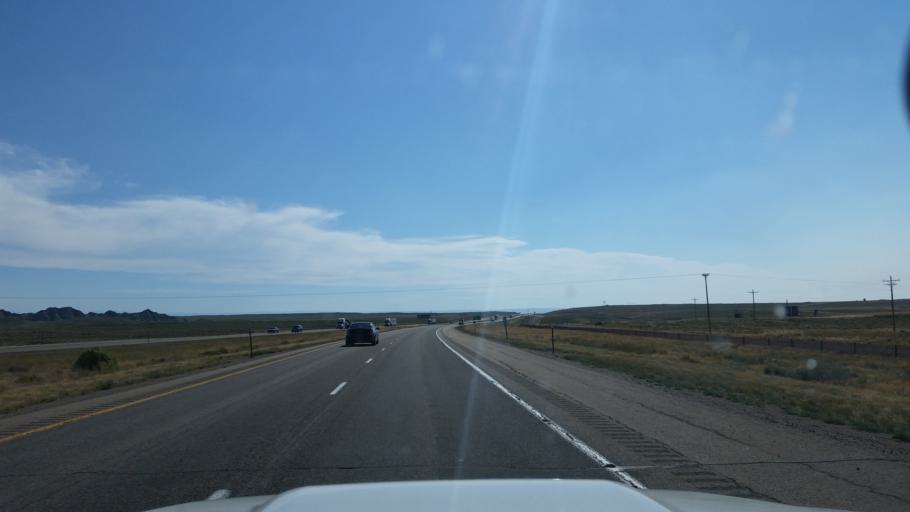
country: US
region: Wyoming
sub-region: Uinta County
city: Lyman
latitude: 41.4383
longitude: -110.0962
